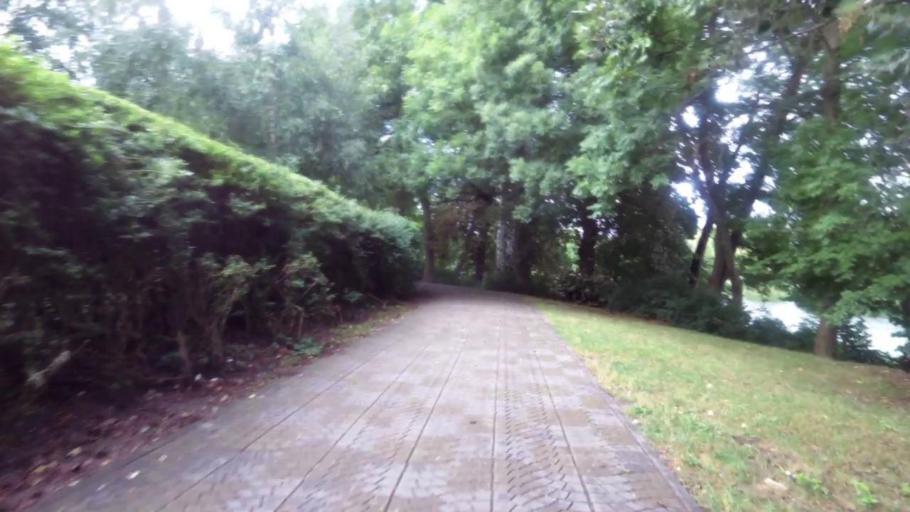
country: PL
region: West Pomeranian Voivodeship
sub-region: Powiat mysliborski
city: Debno
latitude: 52.7420
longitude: 14.7023
